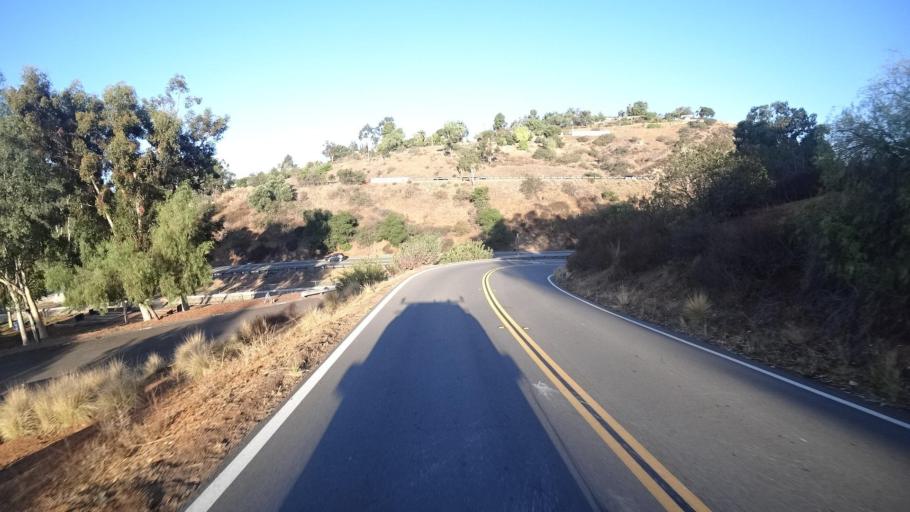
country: US
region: California
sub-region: San Diego County
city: Spring Valley
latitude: 32.7610
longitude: -117.0016
